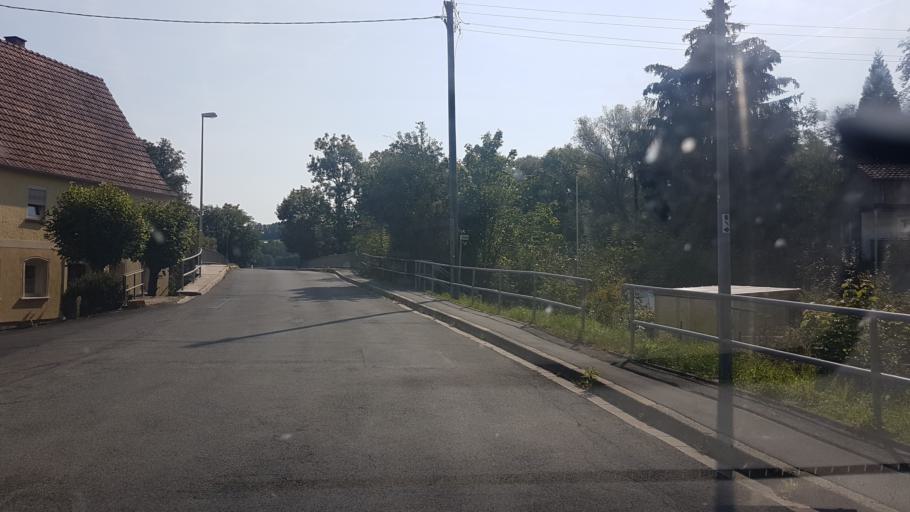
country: DE
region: Bavaria
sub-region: Upper Franconia
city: Kueps Oberfranken
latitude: 50.1871
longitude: 11.2580
